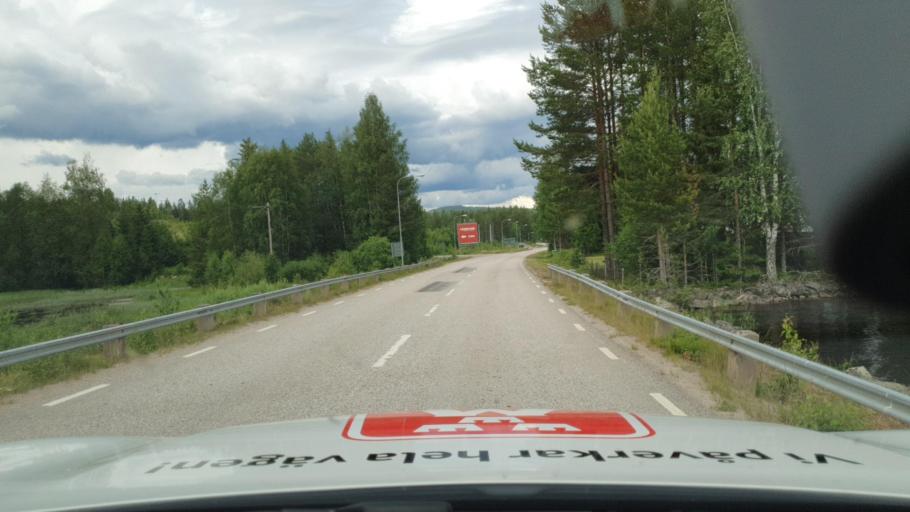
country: NO
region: Hedmark
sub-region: Trysil
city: Innbygda
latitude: 61.0432
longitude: 12.5926
